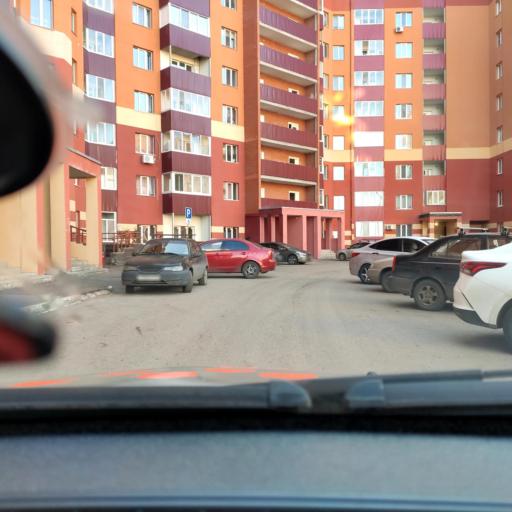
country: RU
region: Bashkortostan
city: Mikhaylovka
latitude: 54.7166
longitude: 55.8415
